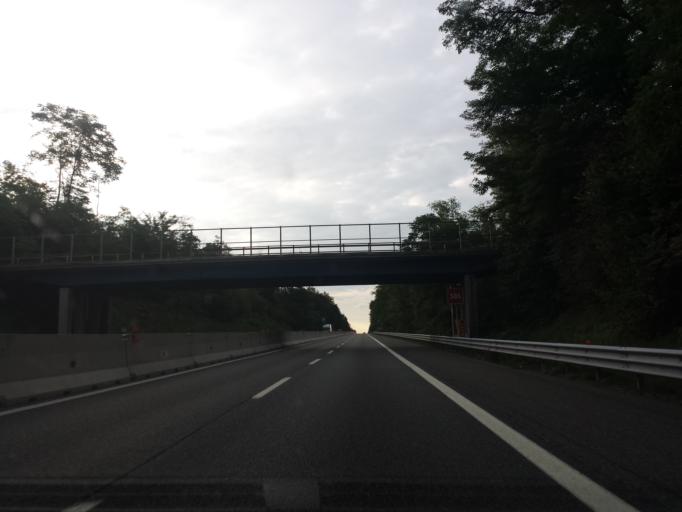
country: IT
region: Lombardy
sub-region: Provincia di Varese
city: Arsago Seprio
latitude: 45.7079
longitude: 8.7248
